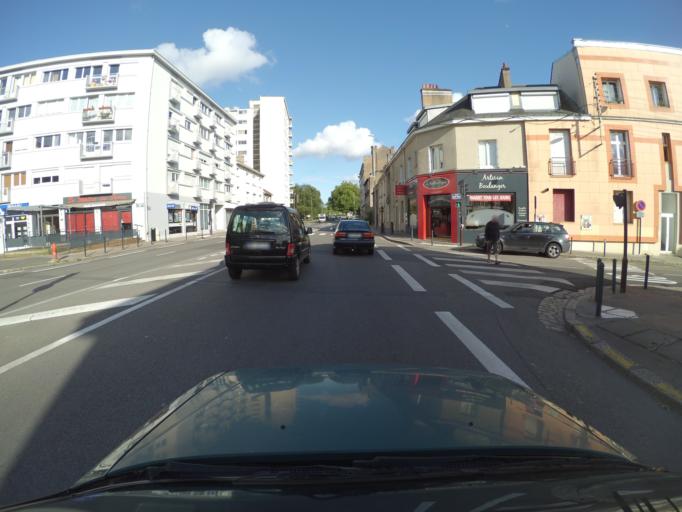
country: FR
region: Pays de la Loire
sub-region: Departement de la Loire-Atlantique
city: Nantes
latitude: 47.2014
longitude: -1.5468
